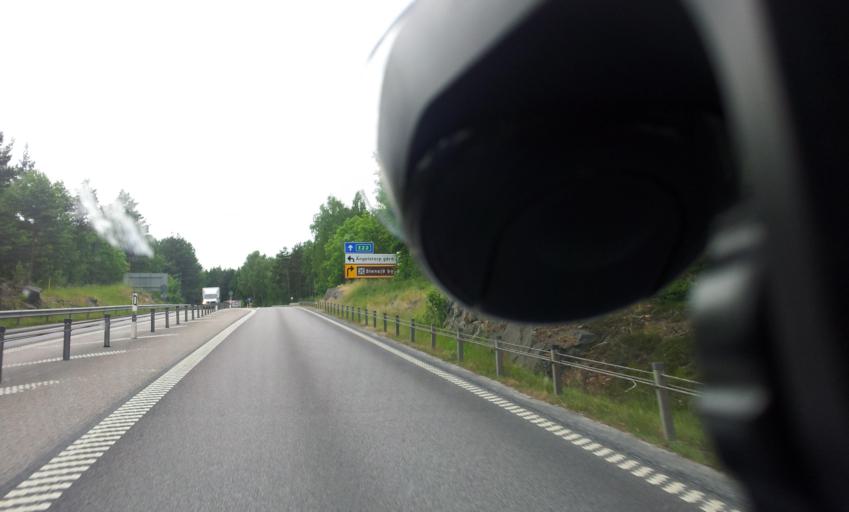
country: SE
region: Kalmar
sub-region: Oskarshamns Kommun
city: Oskarshamn
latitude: 57.3356
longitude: 16.4817
